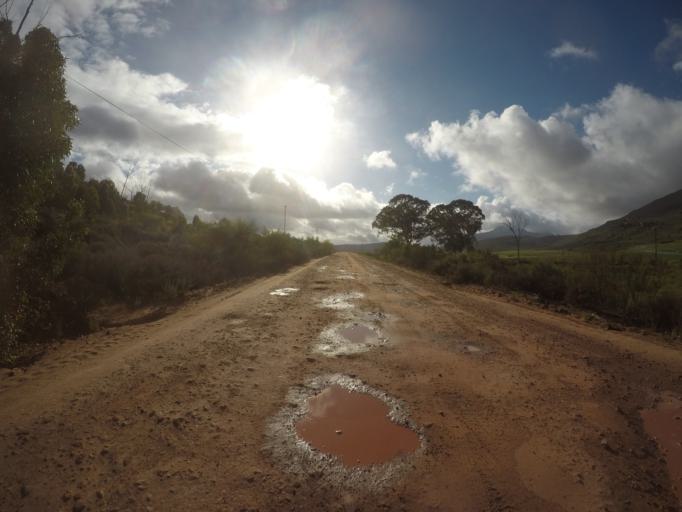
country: ZA
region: Western Cape
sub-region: West Coast District Municipality
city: Clanwilliam
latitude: -32.3435
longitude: 18.8202
